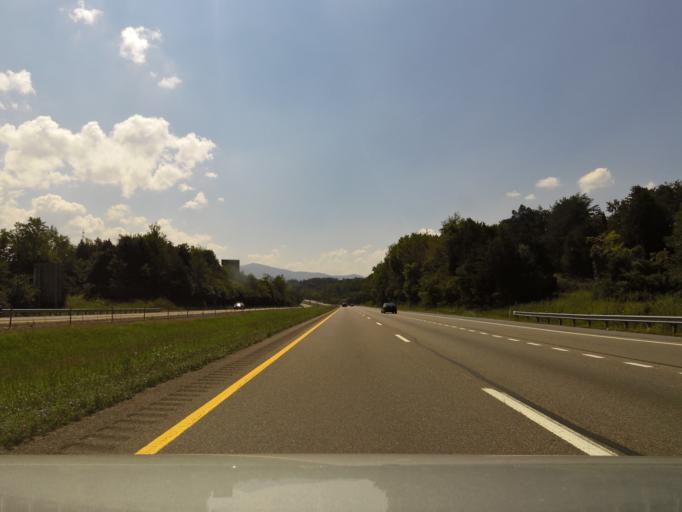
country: US
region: Tennessee
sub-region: Cocke County
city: Newport
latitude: 35.9450
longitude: -83.2021
